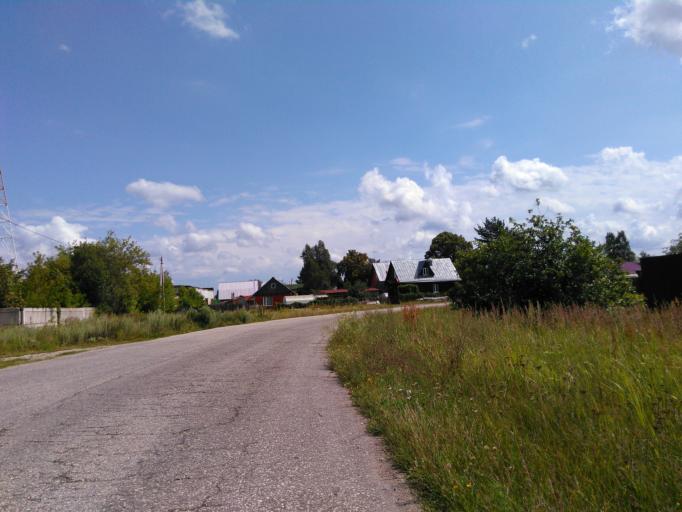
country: RU
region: Vladimir
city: Krasnyy Oktyabr'
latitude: 56.0226
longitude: 38.7979
